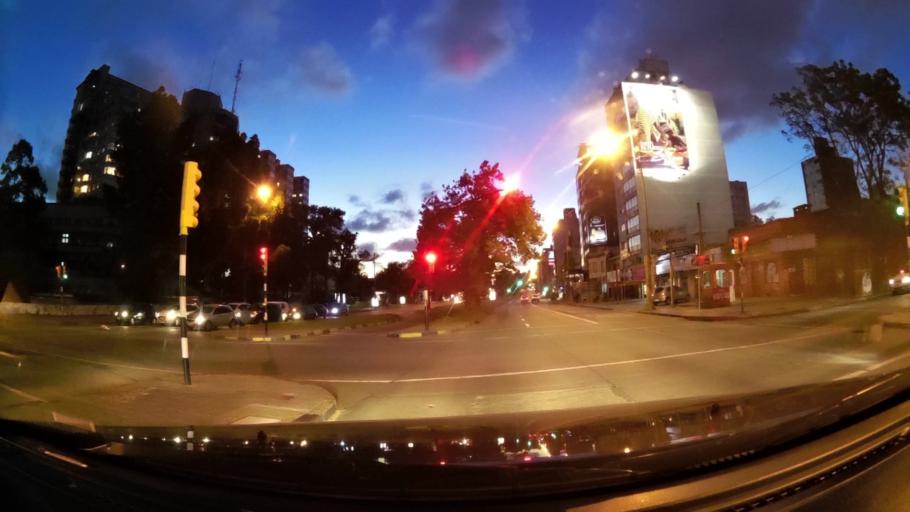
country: UY
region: Montevideo
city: Montevideo
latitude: -34.8900
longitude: -56.1506
